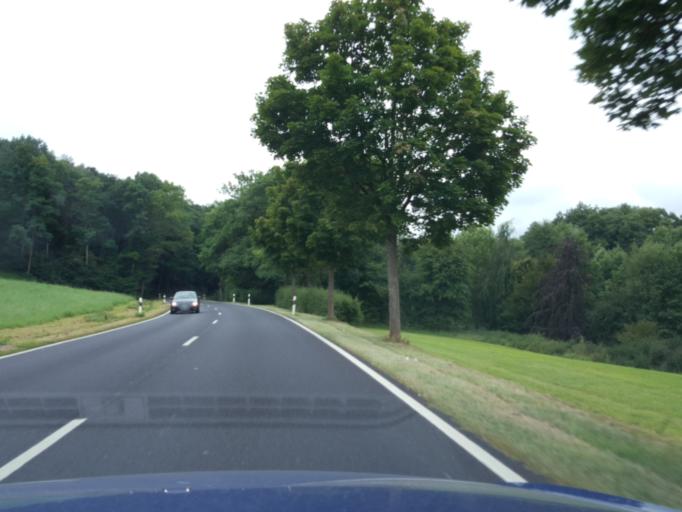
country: LU
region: Luxembourg
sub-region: Canton de Capellen
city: Kehlen
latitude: 49.6522
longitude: 6.0290
